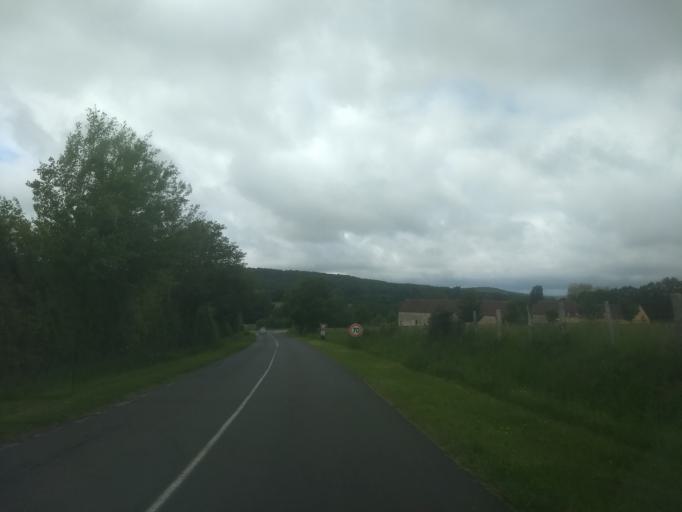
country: FR
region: Lower Normandy
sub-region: Departement de l'Orne
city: Bretoncelles
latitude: 48.4682
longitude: 0.8864
